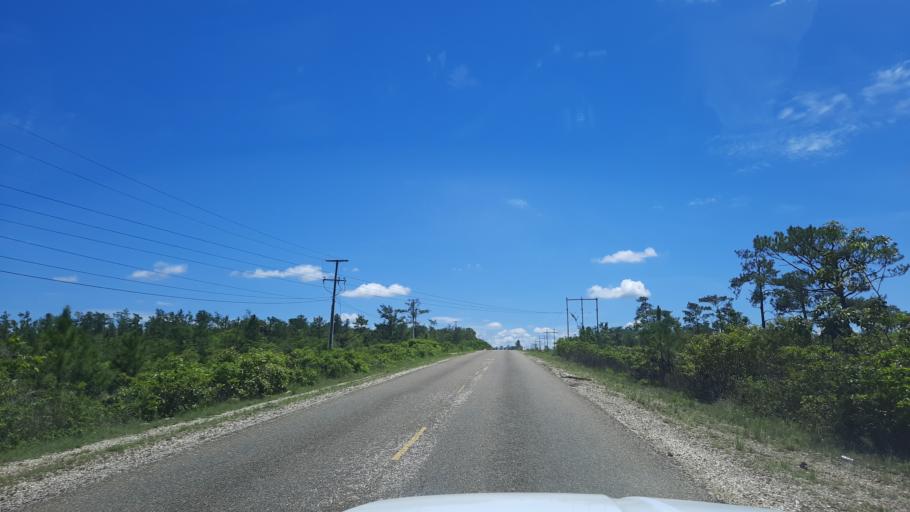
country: BZ
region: Cayo
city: Belmopan
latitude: 17.3476
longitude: -88.5533
